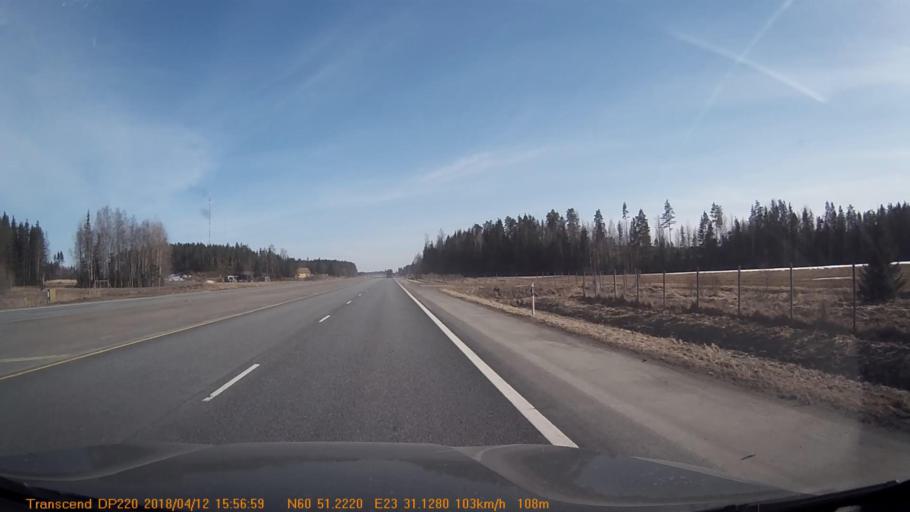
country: FI
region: Haeme
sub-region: Forssa
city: Jokioinen
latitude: 60.8535
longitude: 23.5191
